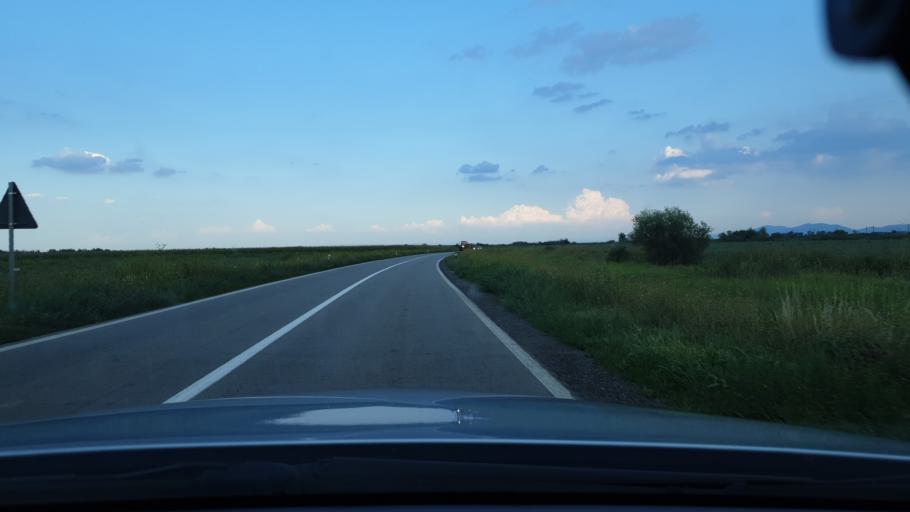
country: RS
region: Autonomna Pokrajina Vojvodina
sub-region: Juznobanatski Okrug
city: Plandiste
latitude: 45.2565
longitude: 21.0886
